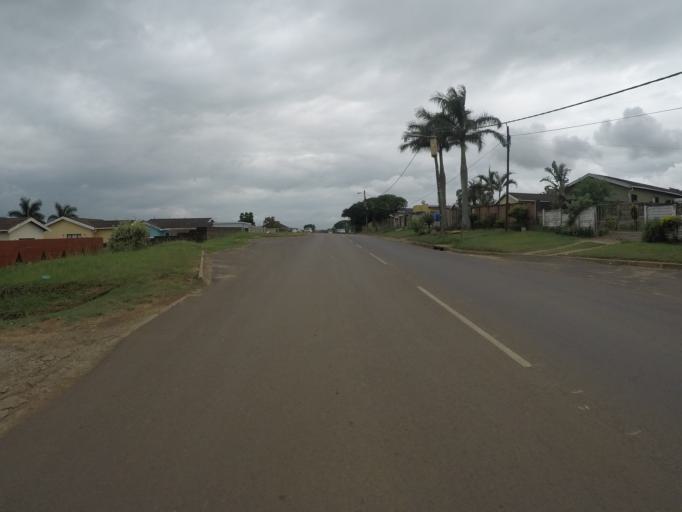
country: ZA
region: KwaZulu-Natal
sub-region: uThungulu District Municipality
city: Empangeni
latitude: -28.7848
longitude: 31.8534
